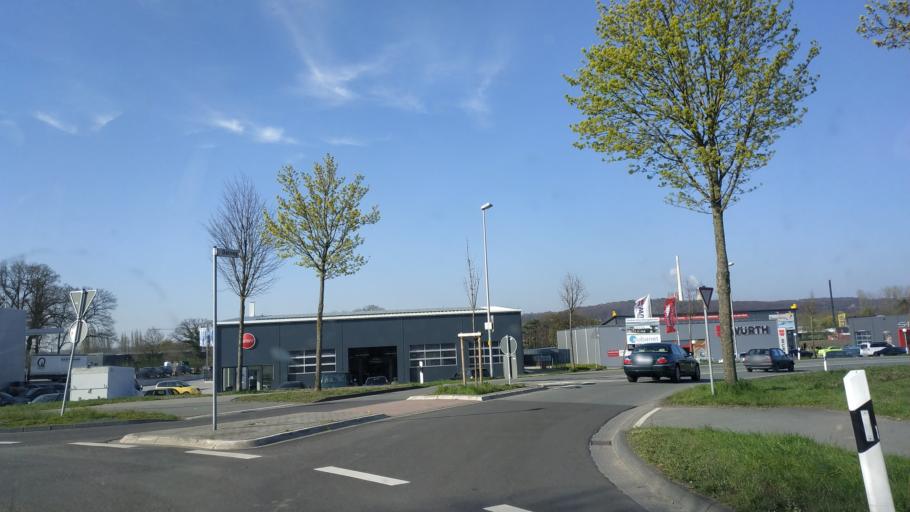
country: DE
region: North Rhine-Westphalia
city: Ibbenburen
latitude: 52.2596
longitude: 7.7273
